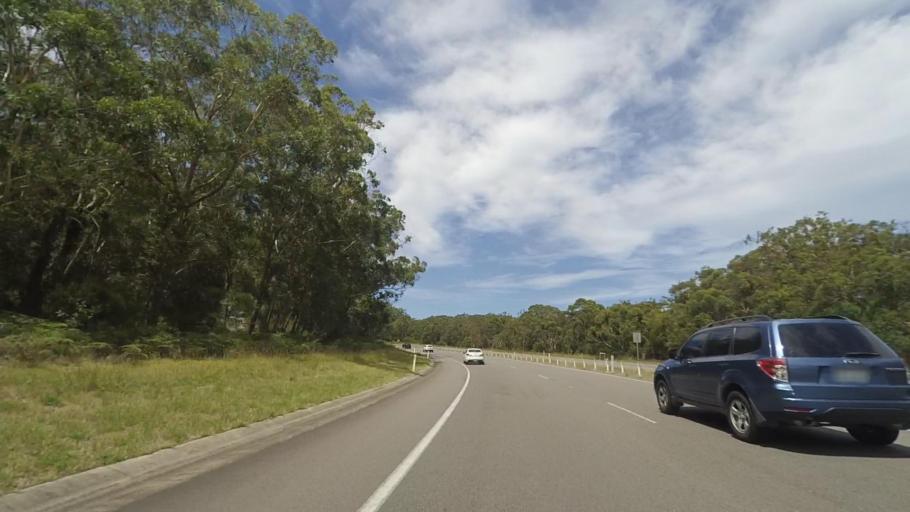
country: AU
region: New South Wales
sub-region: Port Stephens Shire
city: Anna Bay
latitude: -32.7726
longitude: 152.0100
